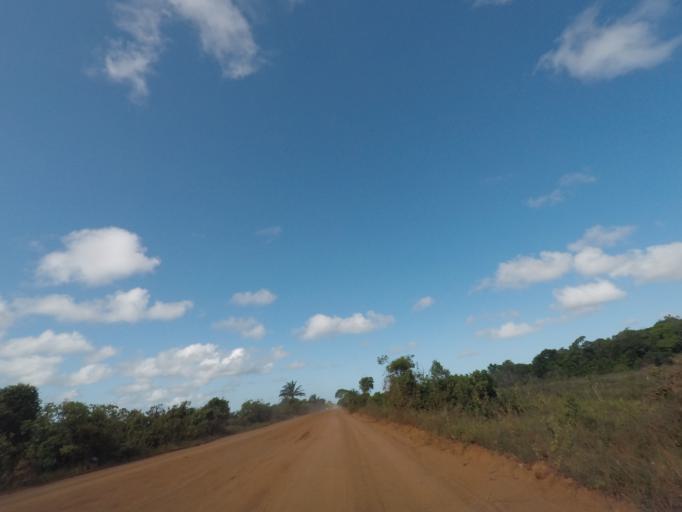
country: BR
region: Bahia
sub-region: Marau
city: Marau
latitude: -14.1629
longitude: -39.0131
